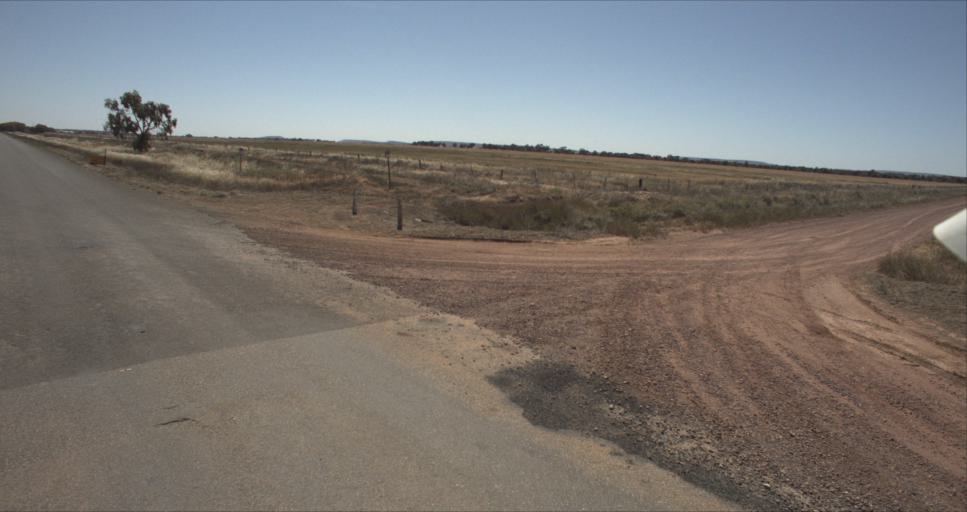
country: AU
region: New South Wales
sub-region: Leeton
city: Leeton
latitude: -34.4931
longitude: 146.2883
